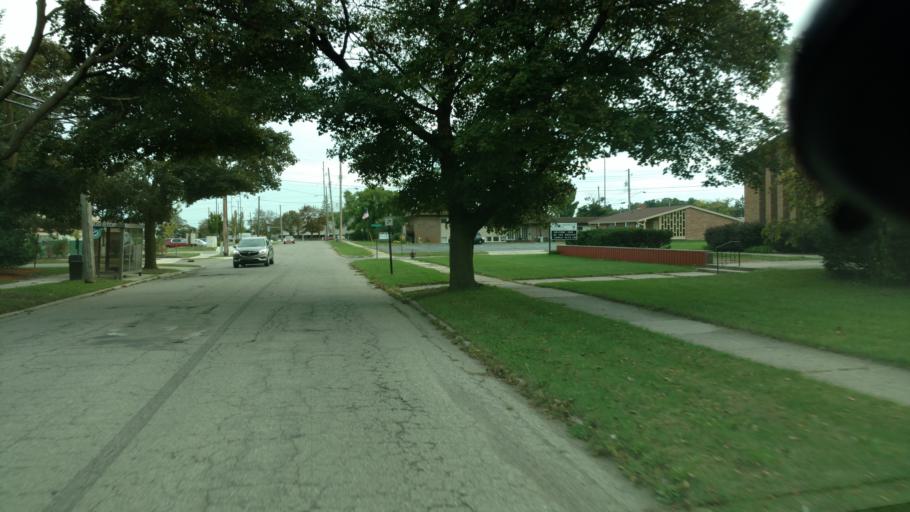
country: US
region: Michigan
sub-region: Ingham County
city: East Lansing
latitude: 42.7448
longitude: -84.5114
